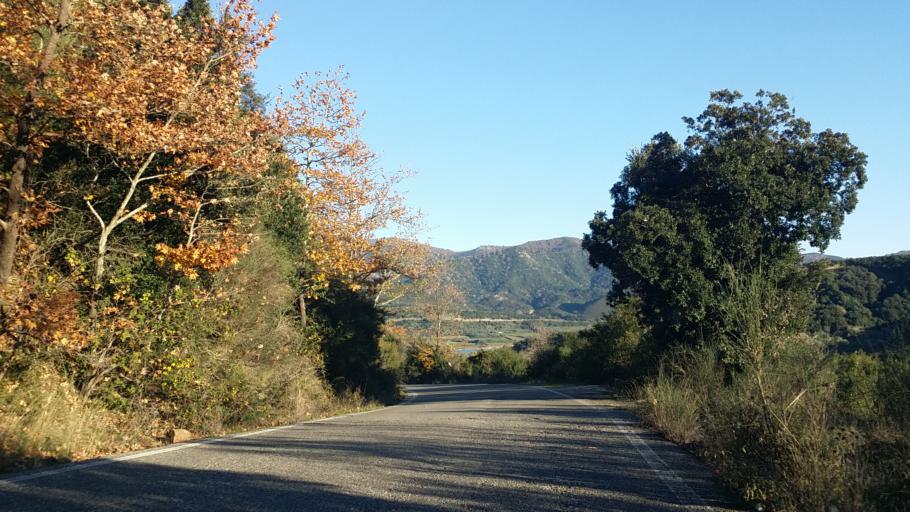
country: GR
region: West Greece
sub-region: Nomos Aitolias kai Akarnanias
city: Sardinia
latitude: 38.8511
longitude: 21.3300
